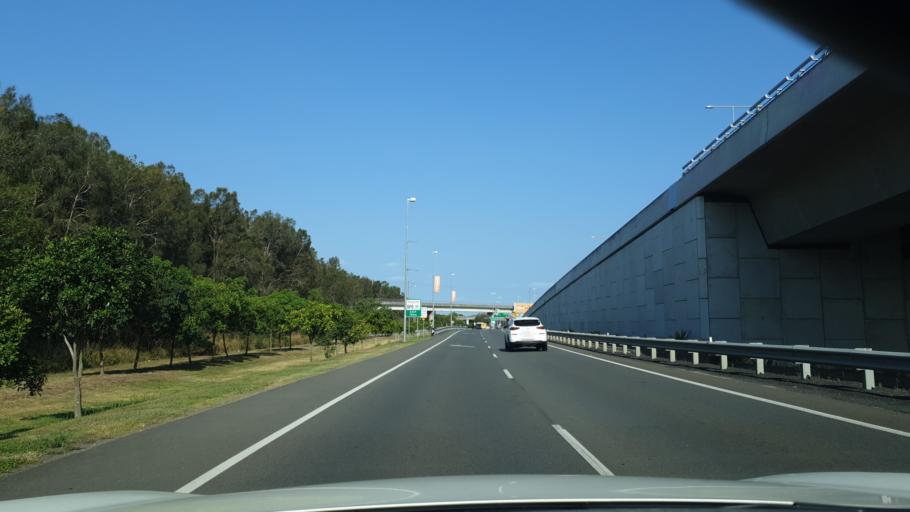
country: AU
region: Queensland
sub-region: Brisbane
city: Ascot
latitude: -27.4121
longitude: 153.0795
